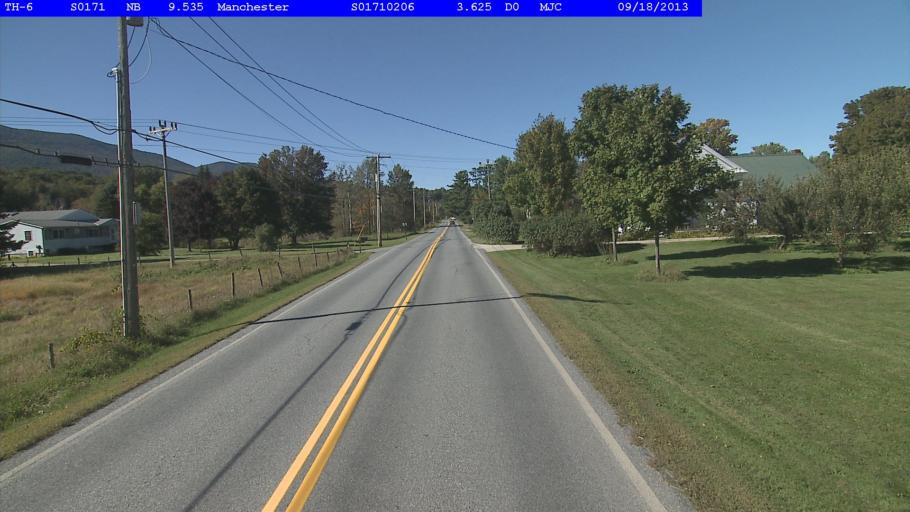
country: US
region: Vermont
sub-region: Bennington County
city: Manchester Center
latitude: 43.1567
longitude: -73.0516
